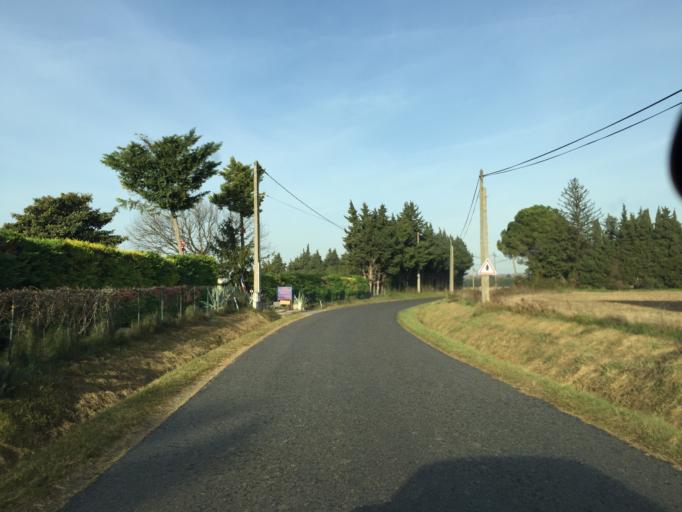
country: FR
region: Provence-Alpes-Cote d'Azur
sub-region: Departement du Vaucluse
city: Orange
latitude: 44.1414
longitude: 4.7879
